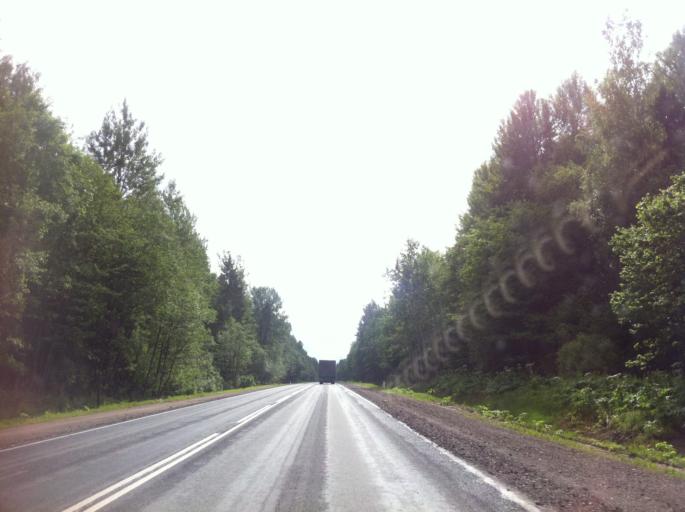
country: RU
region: Pskov
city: Strugi-Krasnyye
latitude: 58.1228
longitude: 29.1364
